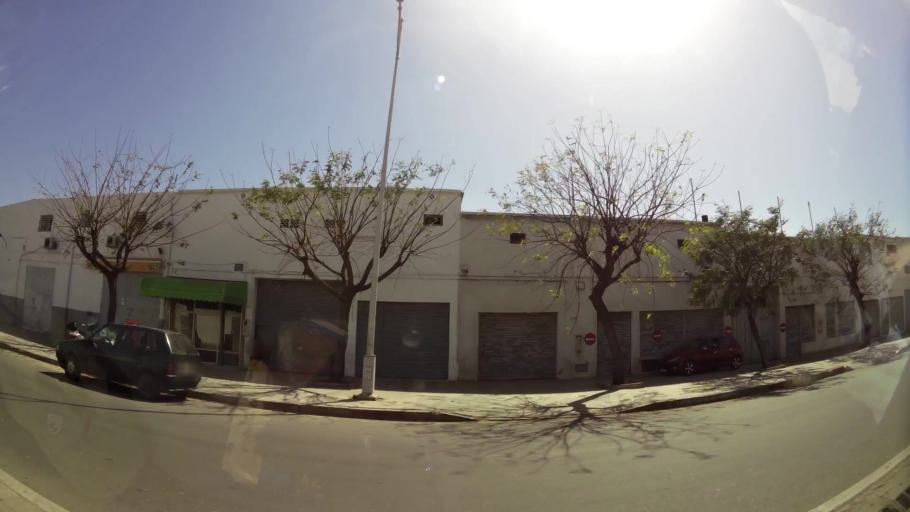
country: MA
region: Oued ed Dahab-Lagouira
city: Dakhla
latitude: 30.4175
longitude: -9.5751
